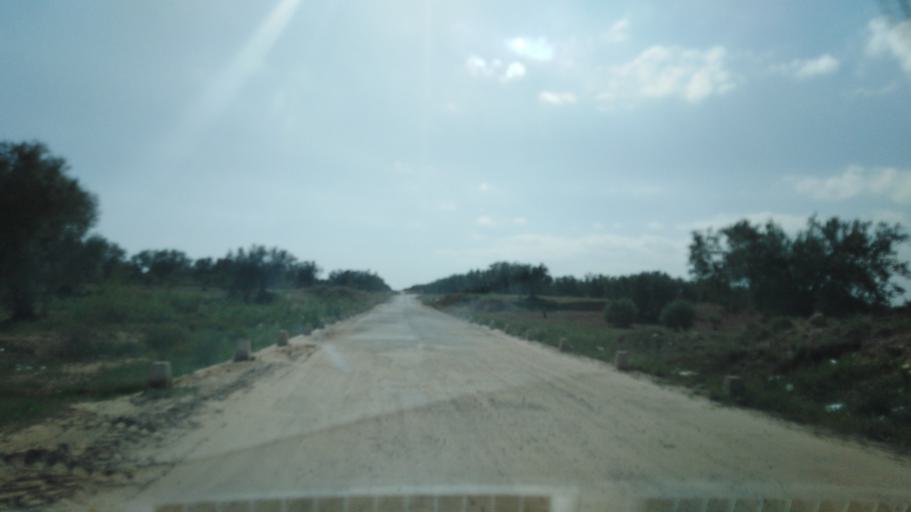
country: TN
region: Safaqis
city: Bi'r `Ali Bin Khalifah
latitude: 34.7770
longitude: 10.3656
